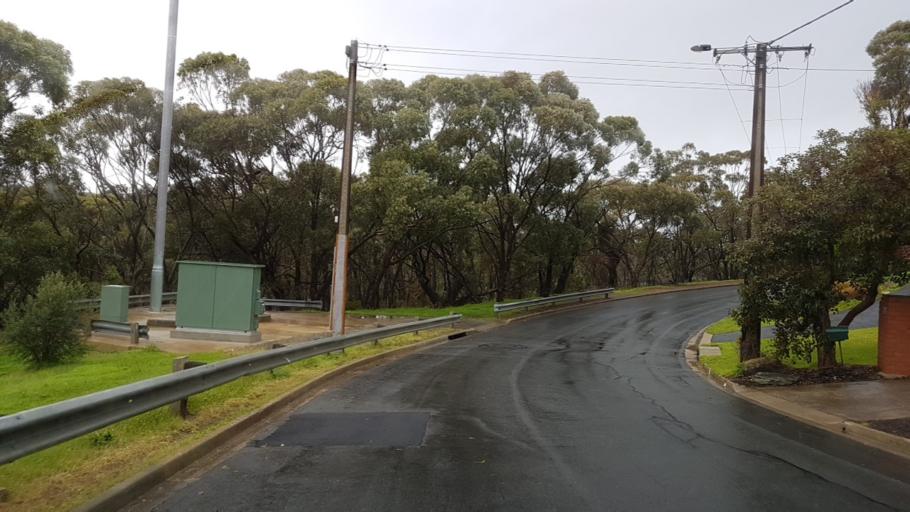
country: AU
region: South Australia
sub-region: Onkaparinga
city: Bedford Park
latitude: -35.0395
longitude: 138.5787
